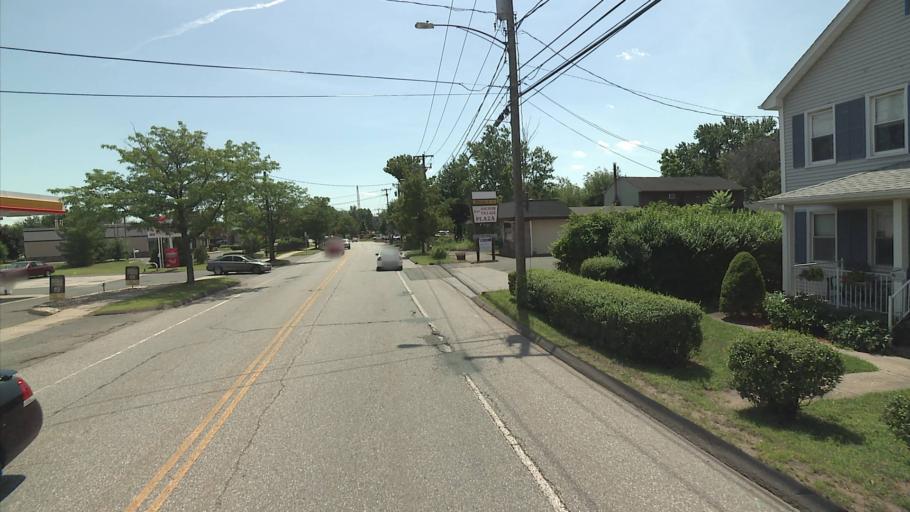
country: US
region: Connecticut
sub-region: Hartford County
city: Kensington
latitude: 41.6277
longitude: -72.7551
